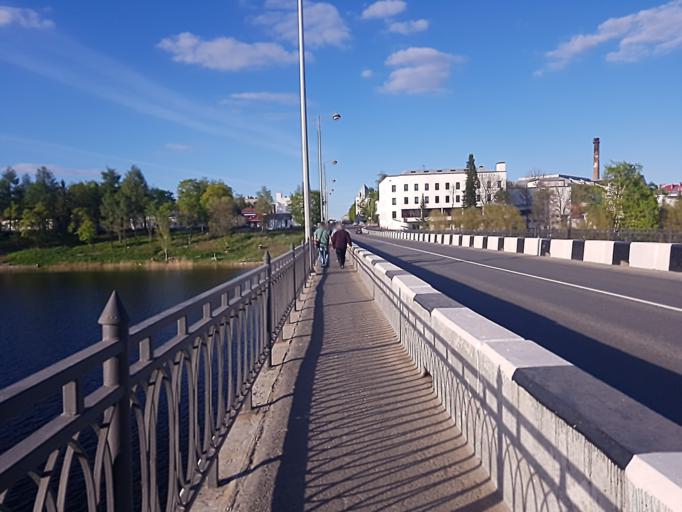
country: RU
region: Republic of Karelia
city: Sortavala
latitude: 61.7004
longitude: 30.6855
